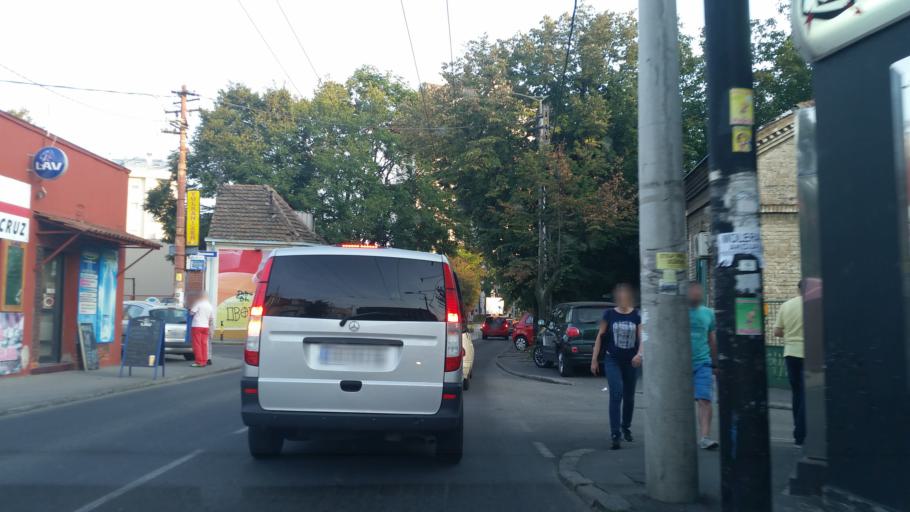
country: RS
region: Central Serbia
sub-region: Belgrade
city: Vracar
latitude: 44.7964
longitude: 20.4895
